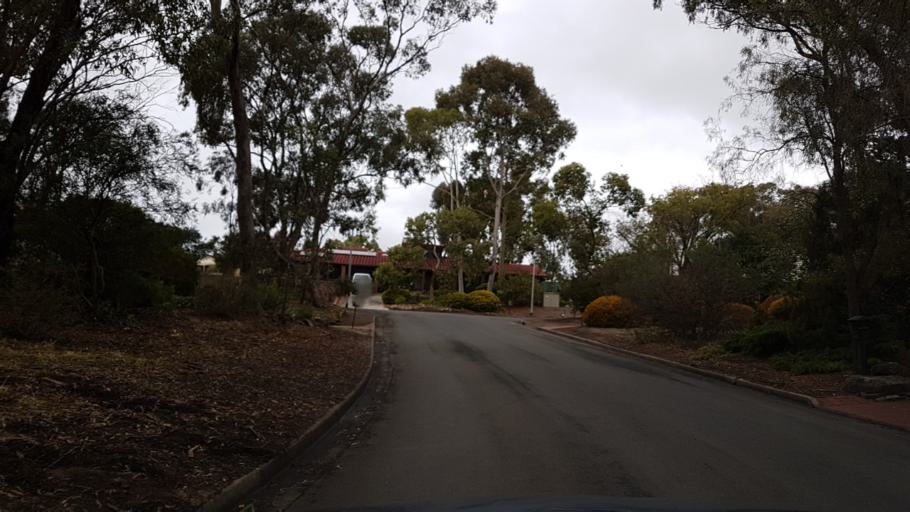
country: AU
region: South Australia
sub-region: Onkaparinga
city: Bedford Park
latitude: -35.0470
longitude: 138.5868
